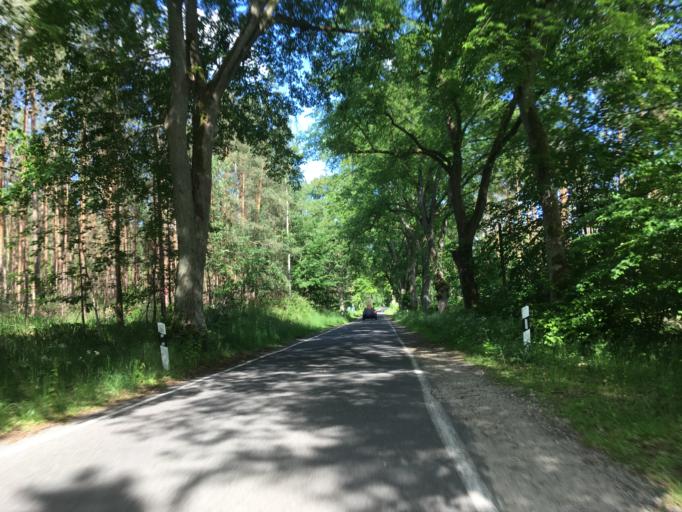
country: DE
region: Brandenburg
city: Joachimsthal
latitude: 52.9932
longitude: 13.7606
